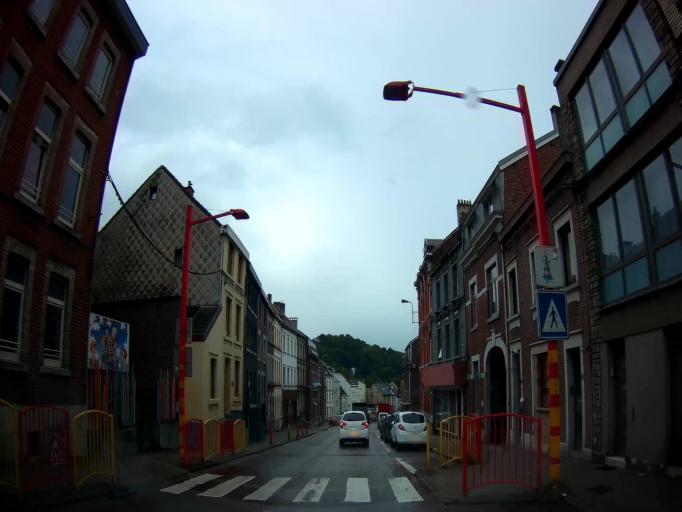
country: BE
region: Wallonia
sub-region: Province de Liege
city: Verviers
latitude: 50.5818
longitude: 5.8430
